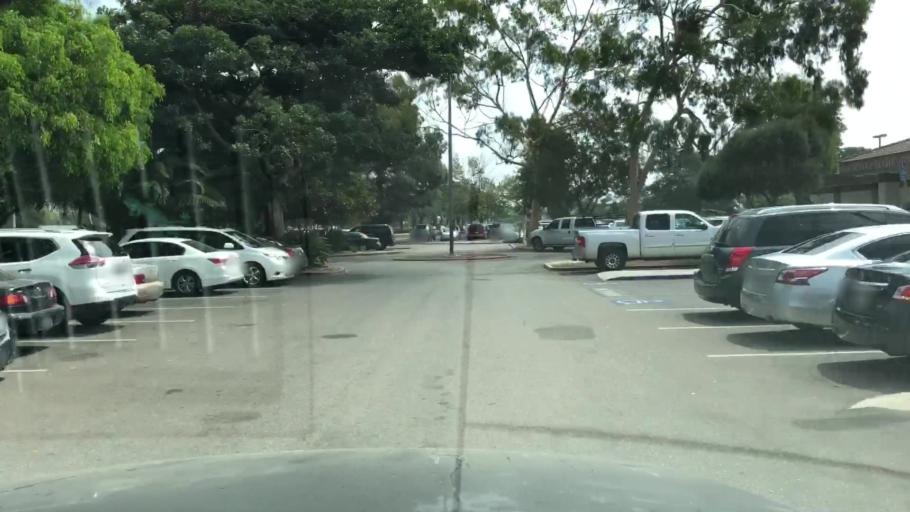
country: US
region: California
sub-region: Ventura County
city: Oxnard
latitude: 34.2065
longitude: -119.1635
